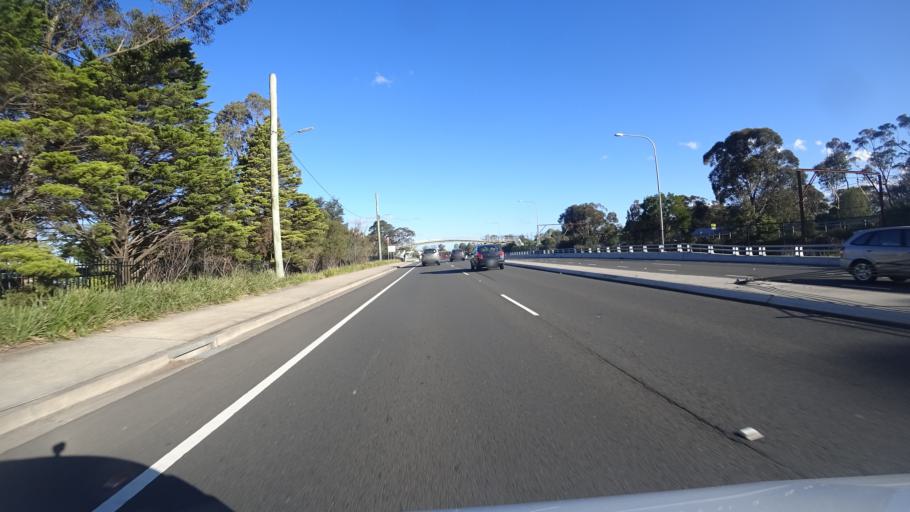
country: AU
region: New South Wales
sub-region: Blue Mountains Municipality
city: Hazelbrook
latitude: -33.7266
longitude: 150.4586
